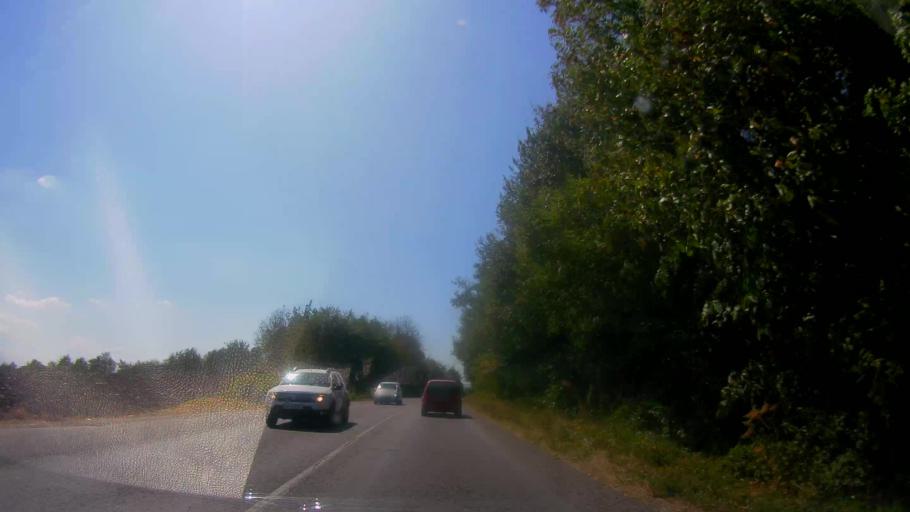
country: BG
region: Veliko Turnovo
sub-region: Obshtina Gorna Oryakhovitsa
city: Purvomaytsi
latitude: 43.2466
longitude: 25.6444
